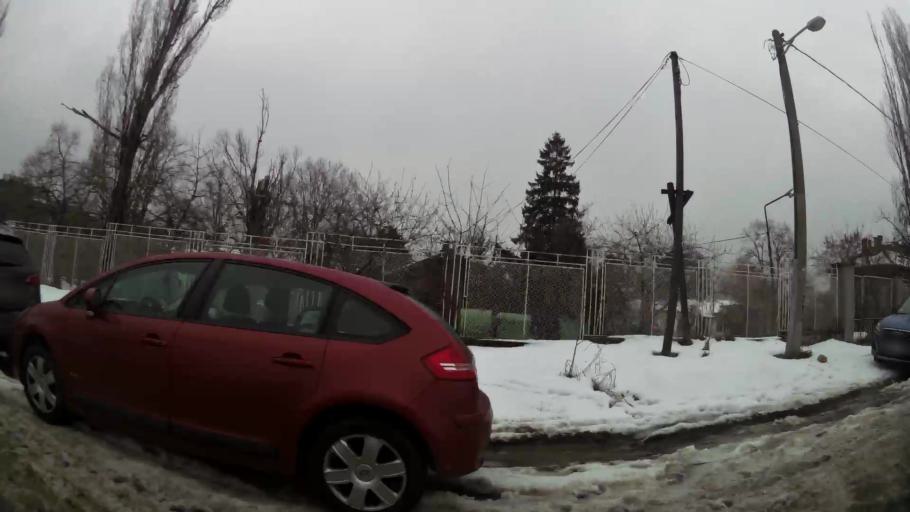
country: RS
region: Central Serbia
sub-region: Belgrade
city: Vozdovac
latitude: 44.7475
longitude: 20.4960
